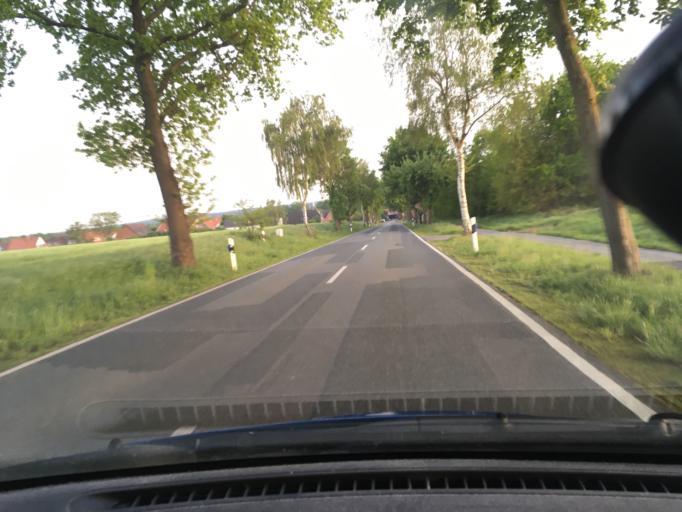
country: DE
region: Lower Saxony
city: Wulfsen
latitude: 53.3107
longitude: 10.1465
